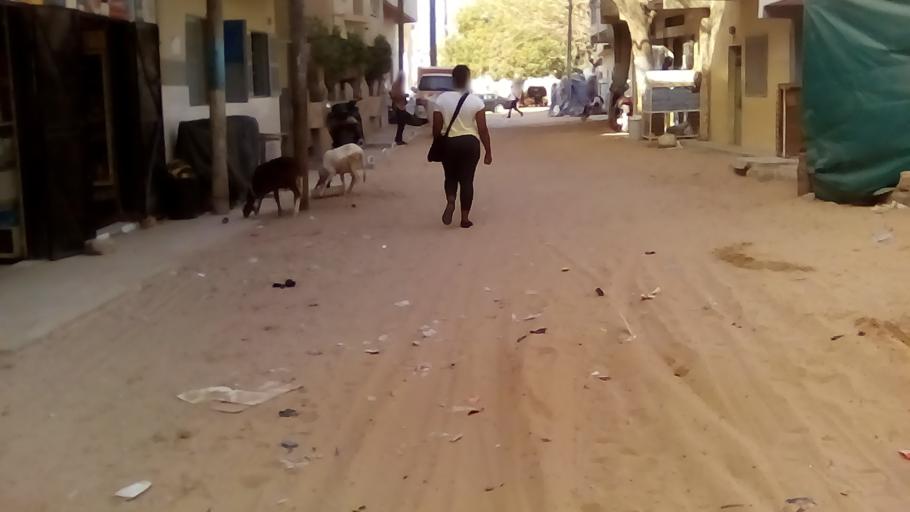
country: SN
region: Dakar
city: Grand Dakar
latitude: 14.7045
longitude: -17.4567
